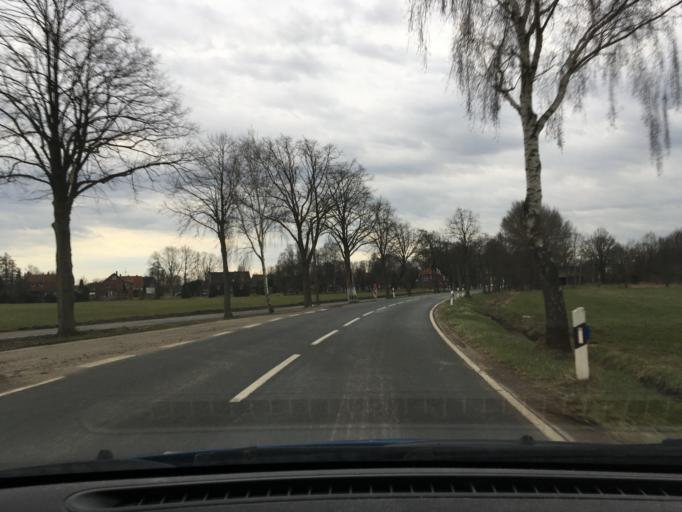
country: DE
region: Lower Saxony
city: Handorf
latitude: 53.3702
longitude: 10.3328
